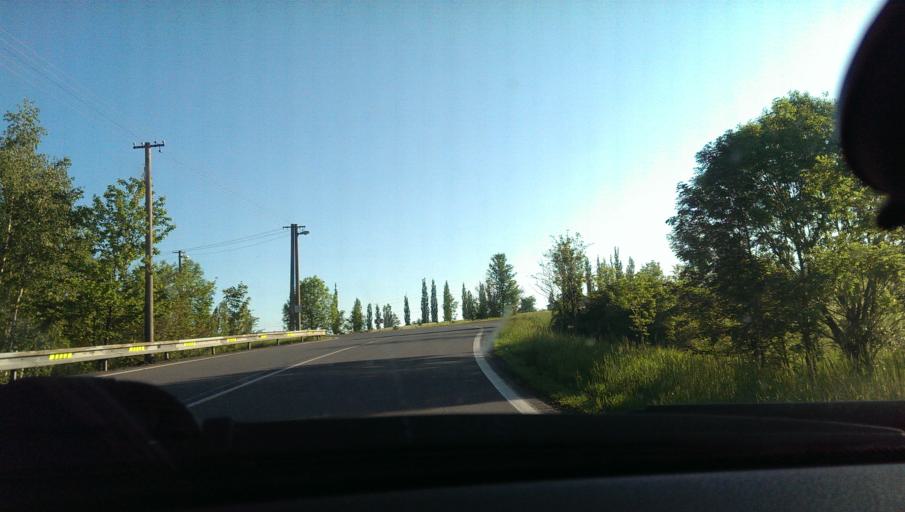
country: CZ
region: Moravskoslezsky
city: Frenstat pod Radhostem
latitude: 49.5538
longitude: 18.2172
